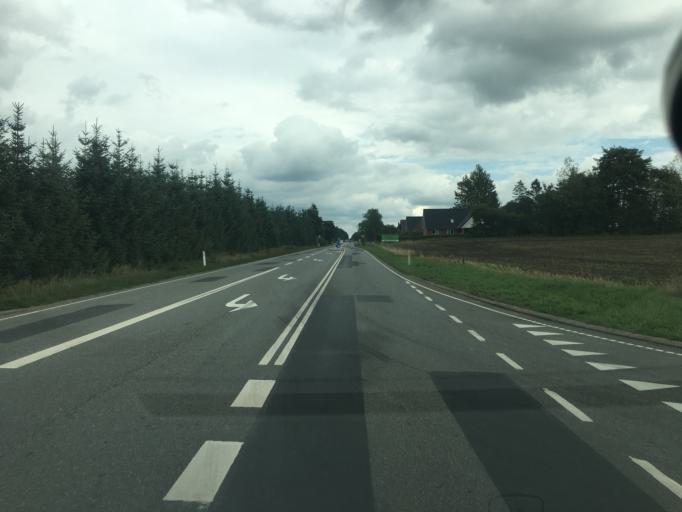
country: DK
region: South Denmark
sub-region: Tonder Kommune
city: Toftlund
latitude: 55.1251
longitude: 9.1191
